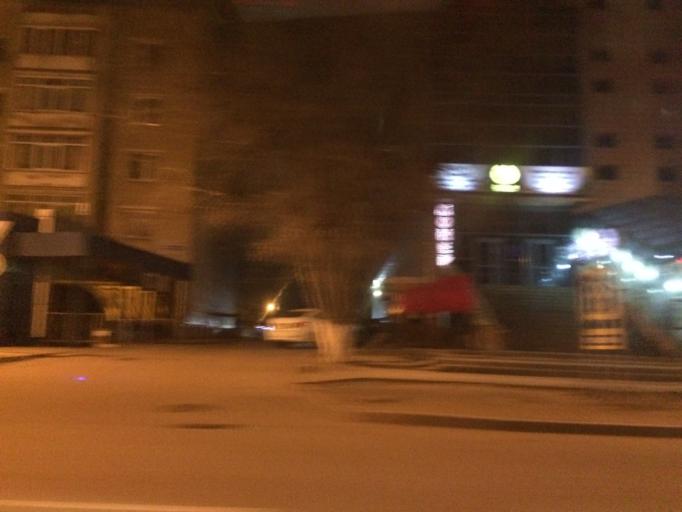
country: KZ
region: Astana Qalasy
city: Astana
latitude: 51.1731
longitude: 71.4253
